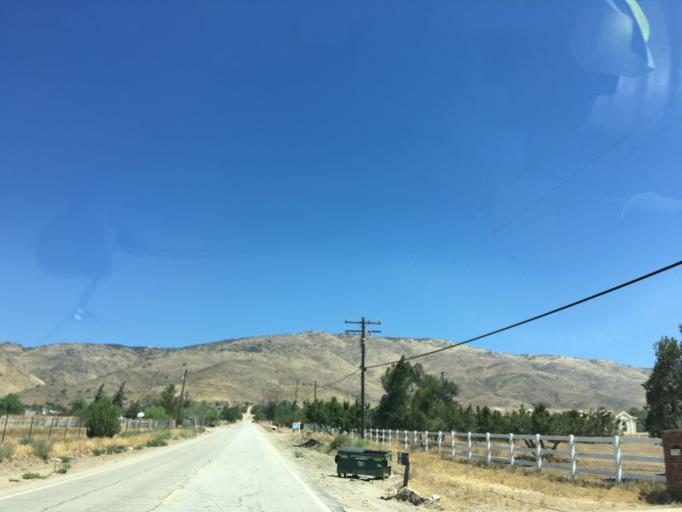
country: US
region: California
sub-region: Los Angeles County
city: Acton
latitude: 34.5199
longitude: -118.2380
